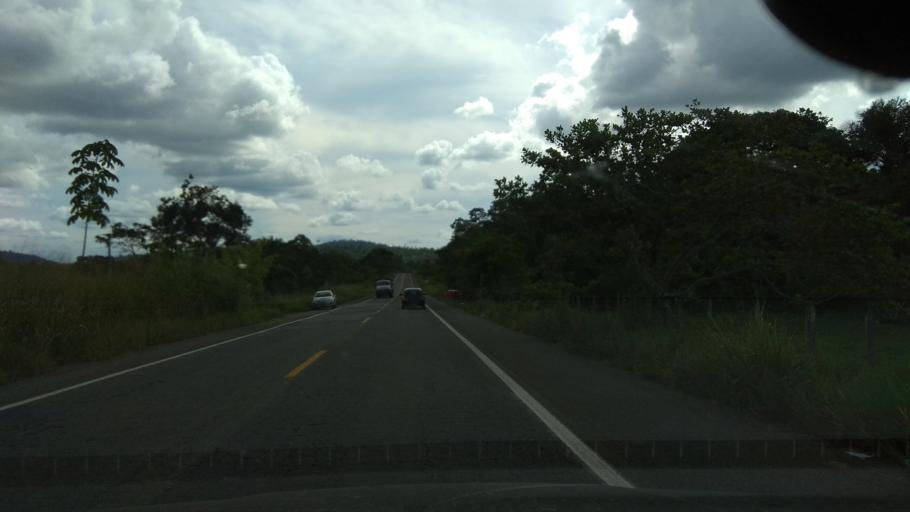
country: BR
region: Bahia
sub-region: Ubaitaba
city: Ubaitaba
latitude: -14.2604
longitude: -39.3461
